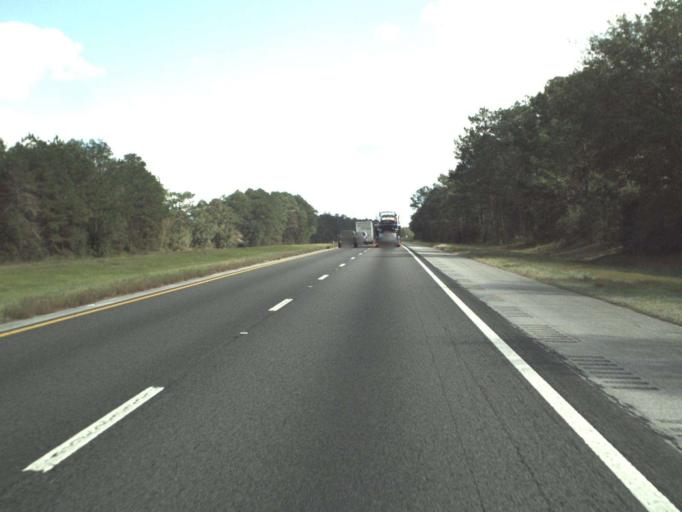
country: US
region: Florida
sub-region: Jackson County
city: Sneads
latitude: 30.6735
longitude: -85.0714
